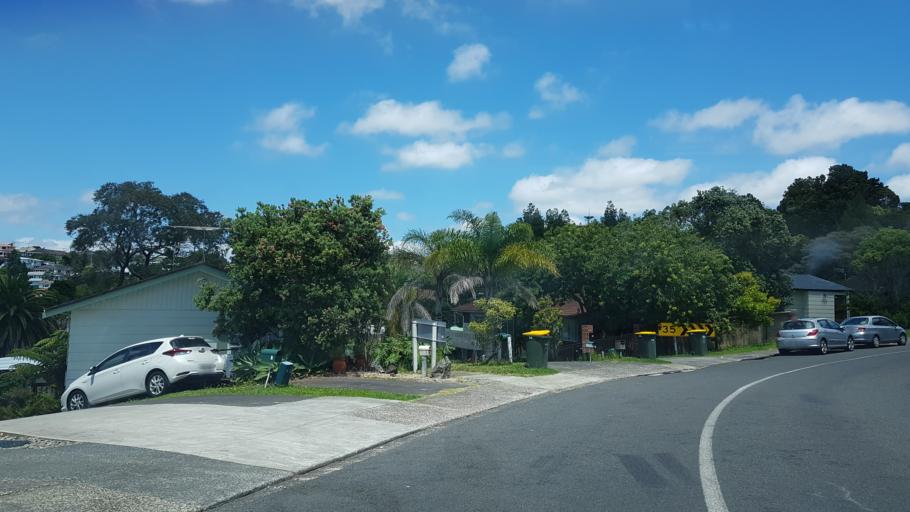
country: NZ
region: Auckland
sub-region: Auckland
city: North Shore
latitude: -36.7878
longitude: 174.7251
